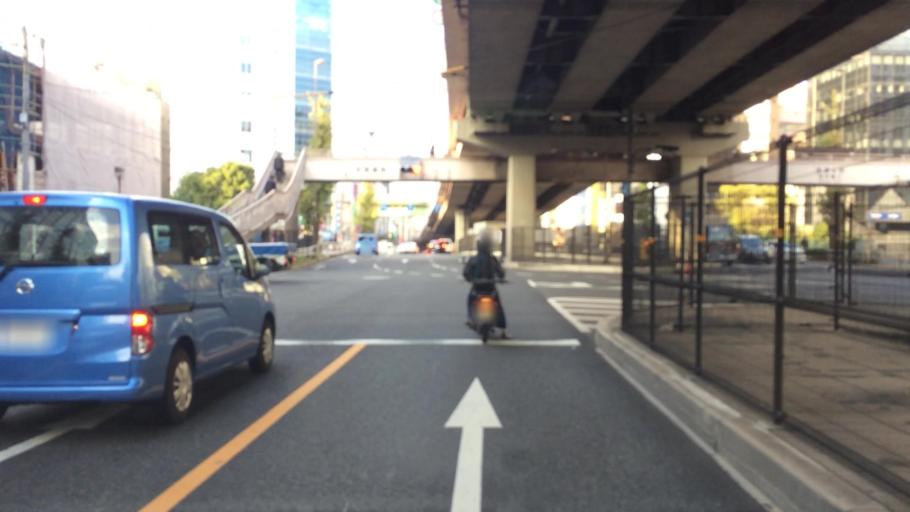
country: JP
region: Tokyo
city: Tokyo
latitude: 35.6962
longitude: 139.7752
